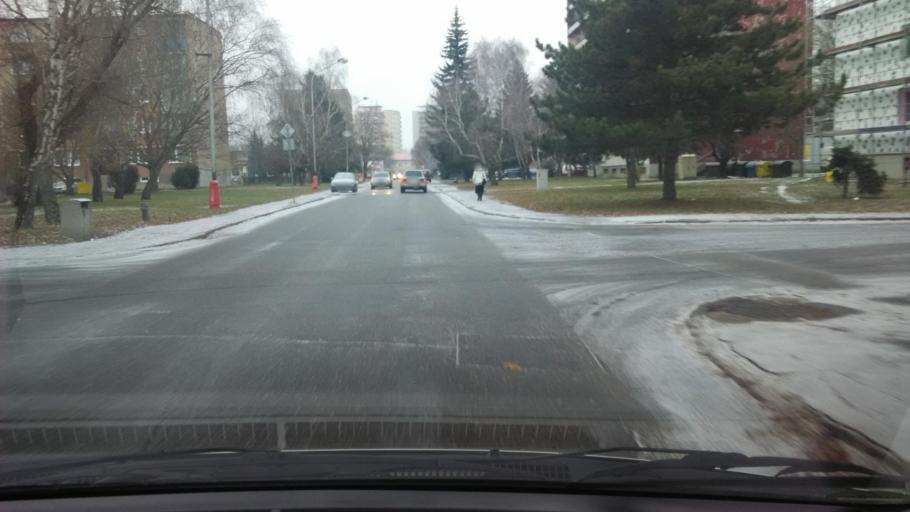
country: SK
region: Nitriansky
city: Levice
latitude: 48.2130
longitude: 18.6017
